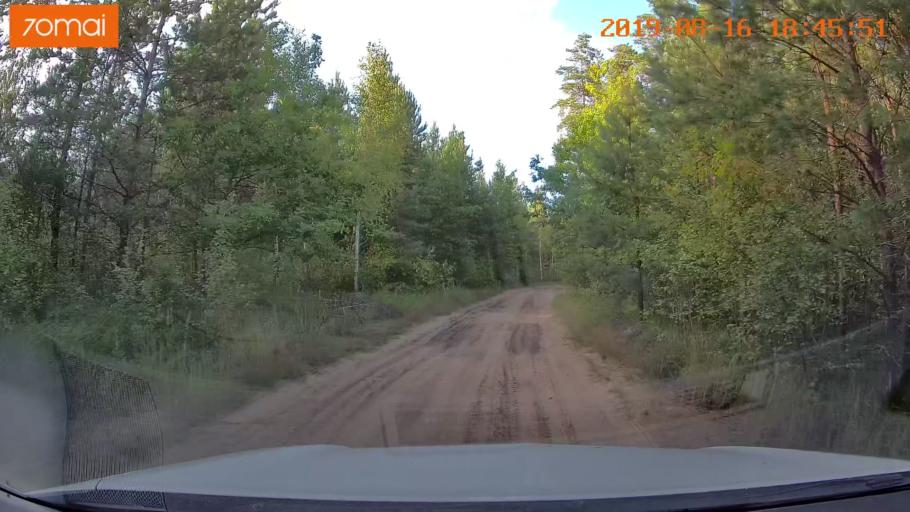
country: BY
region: Mogilev
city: Asipovichy
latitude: 53.2265
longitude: 28.6589
